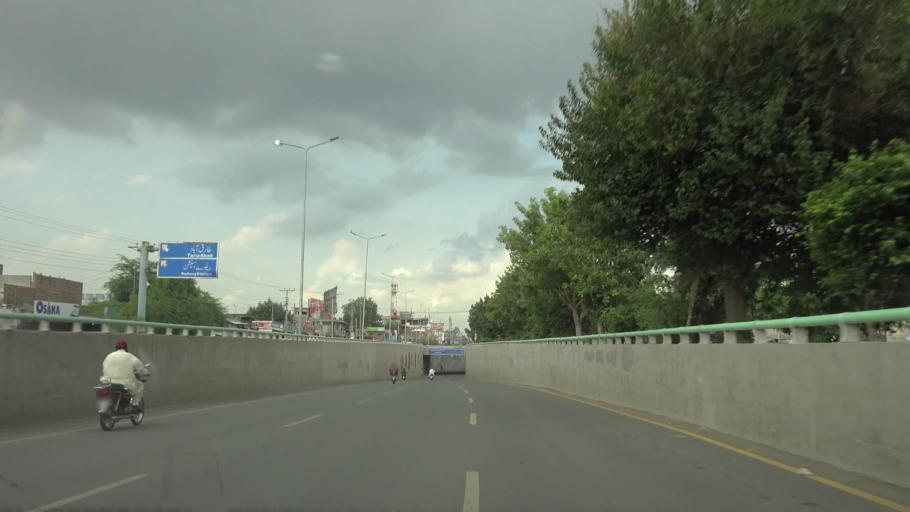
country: PK
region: Punjab
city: Faisalabad
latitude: 31.4246
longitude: 73.1125
